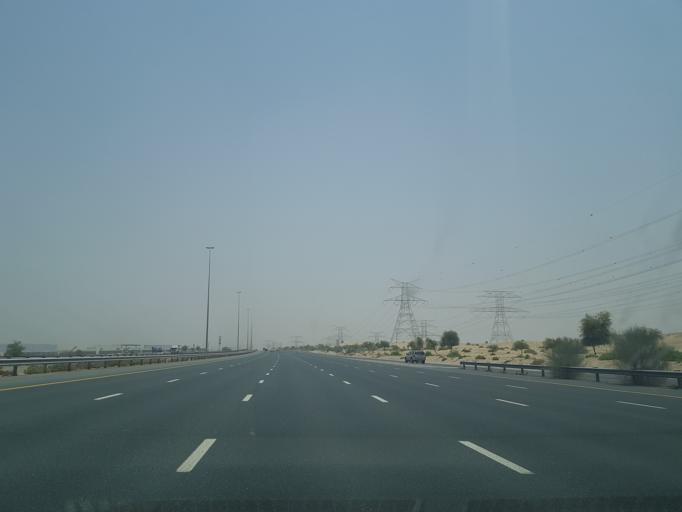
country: AE
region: Dubai
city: Dubai
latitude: 25.0676
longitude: 55.3542
